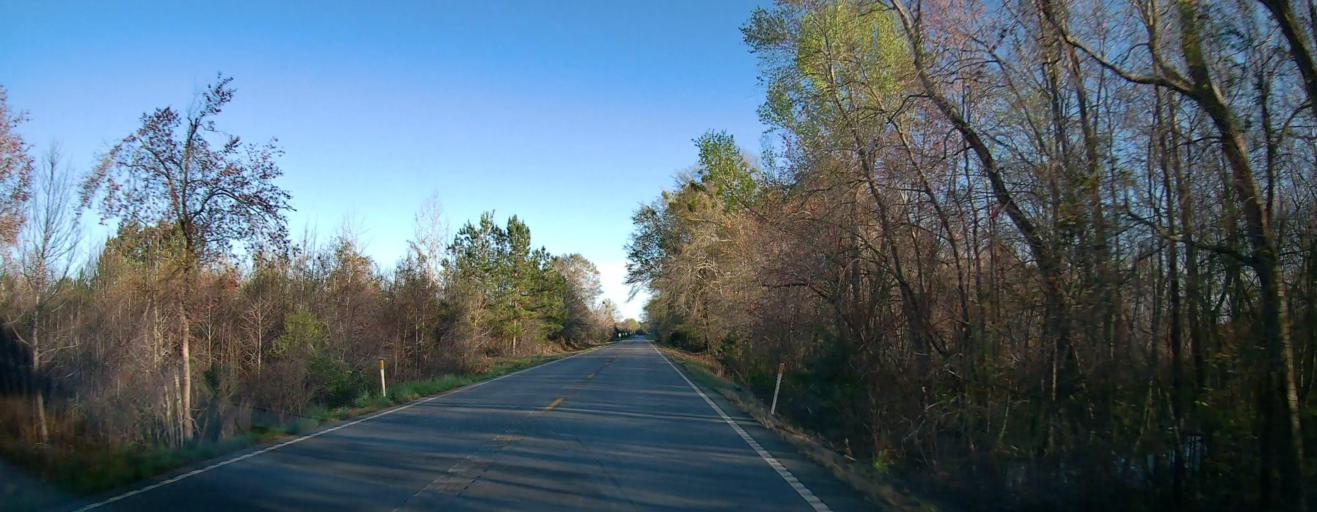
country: US
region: Georgia
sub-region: Wilcox County
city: Abbeville
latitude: 32.1197
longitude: -83.3269
